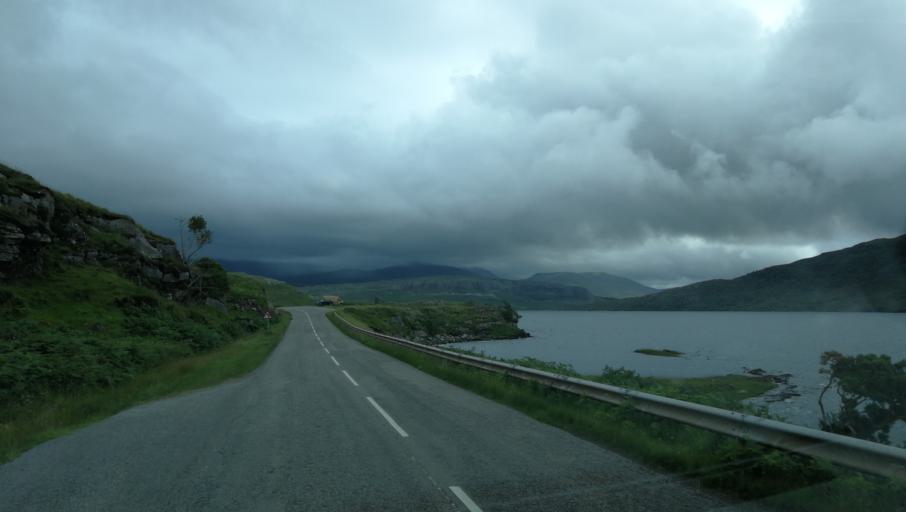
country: GB
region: Scotland
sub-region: Highland
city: Ullapool
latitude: 58.1711
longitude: -5.0003
